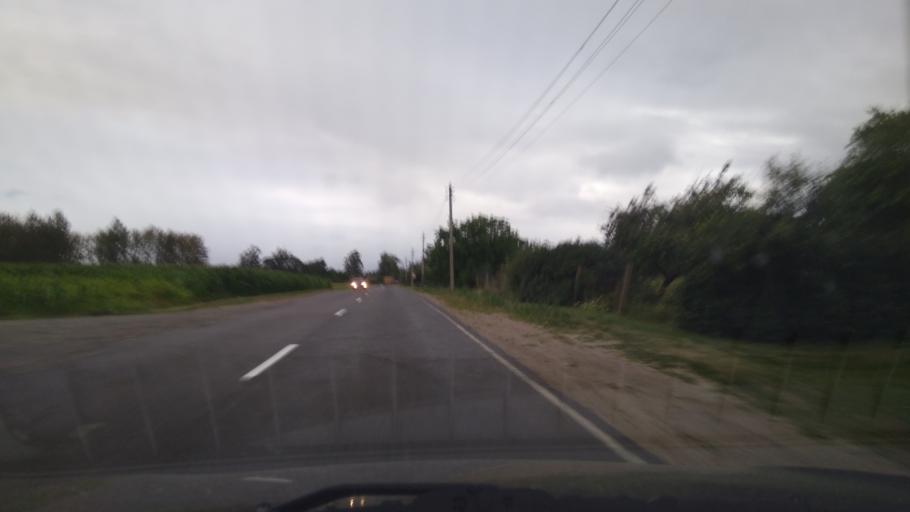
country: BY
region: Brest
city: Byaroza
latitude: 52.4533
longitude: 24.9700
